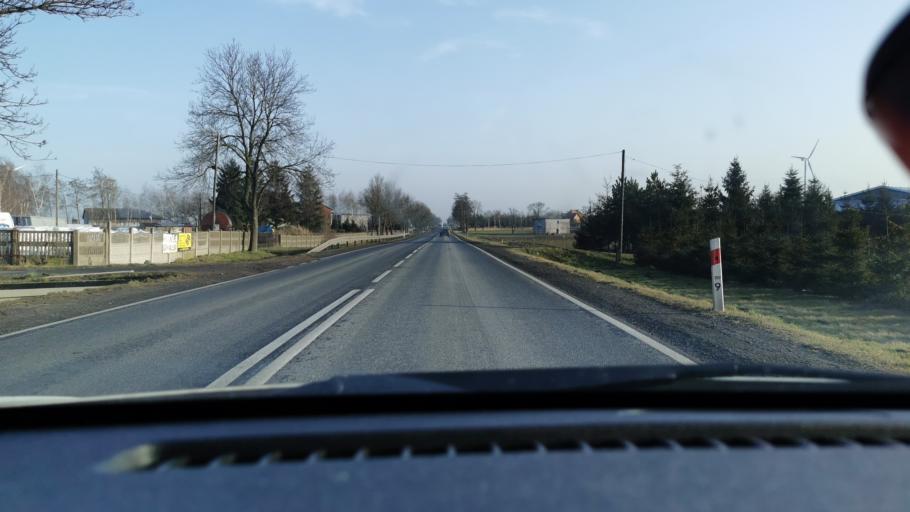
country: PL
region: Lodz Voivodeship
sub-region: Powiat sieradzki
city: Blaszki
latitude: 51.6660
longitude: 18.3868
